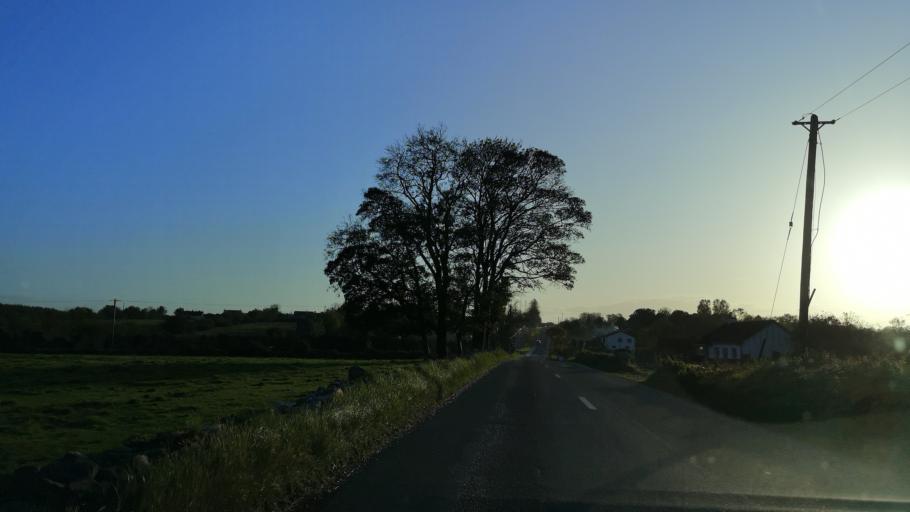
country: IE
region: Connaught
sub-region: Roscommon
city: Castlerea
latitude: 53.7607
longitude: -8.5114
